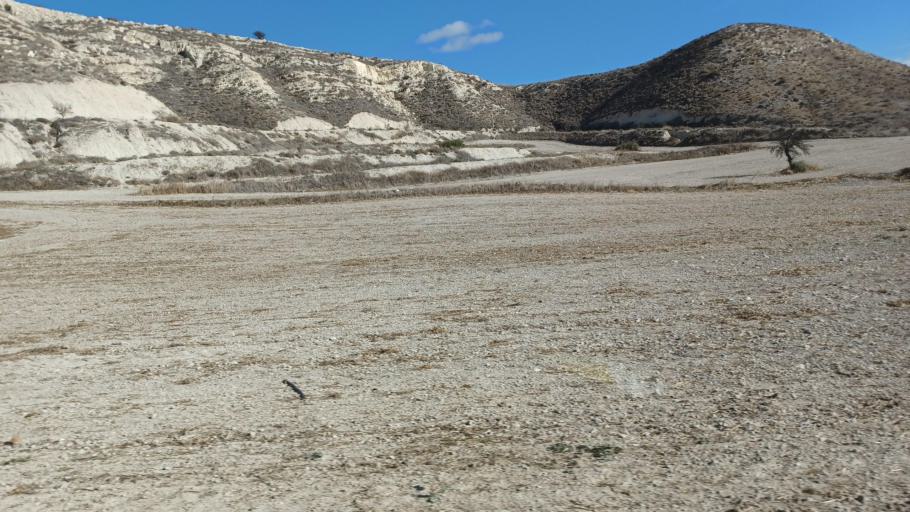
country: CY
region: Larnaka
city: Troulloi
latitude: 35.0306
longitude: 33.5786
